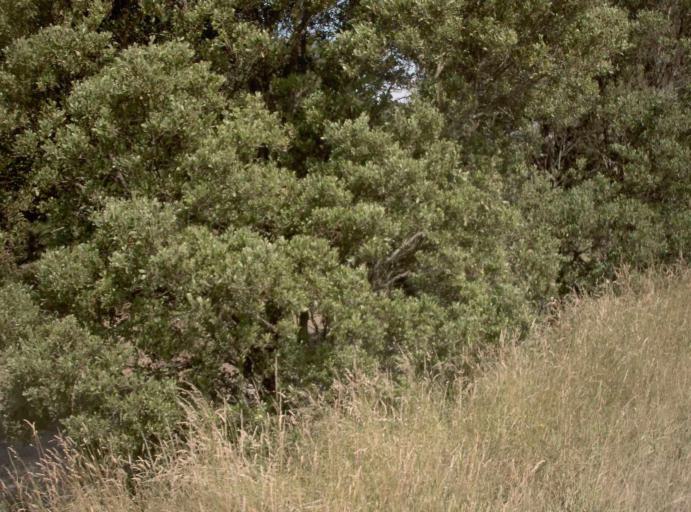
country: AU
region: Victoria
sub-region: Baw Baw
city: Warragul
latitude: -38.3321
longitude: 145.7667
